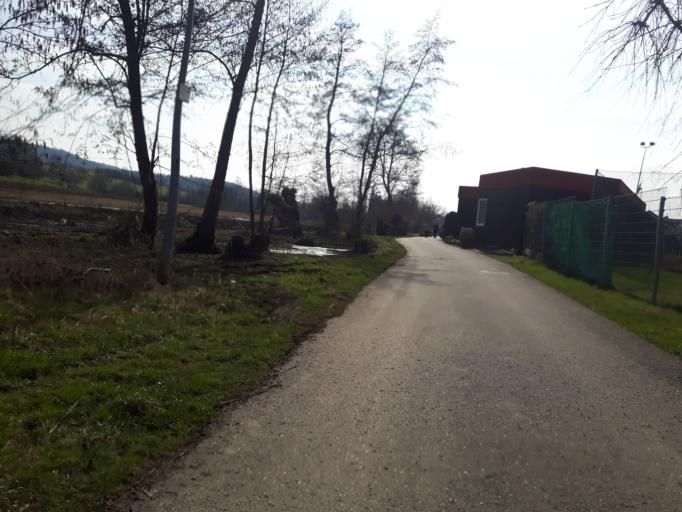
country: DE
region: Baden-Wuerttemberg
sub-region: Regierungsbezirk Stuttgart
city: Gemmingen
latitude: 49.1328
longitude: 9.0157
